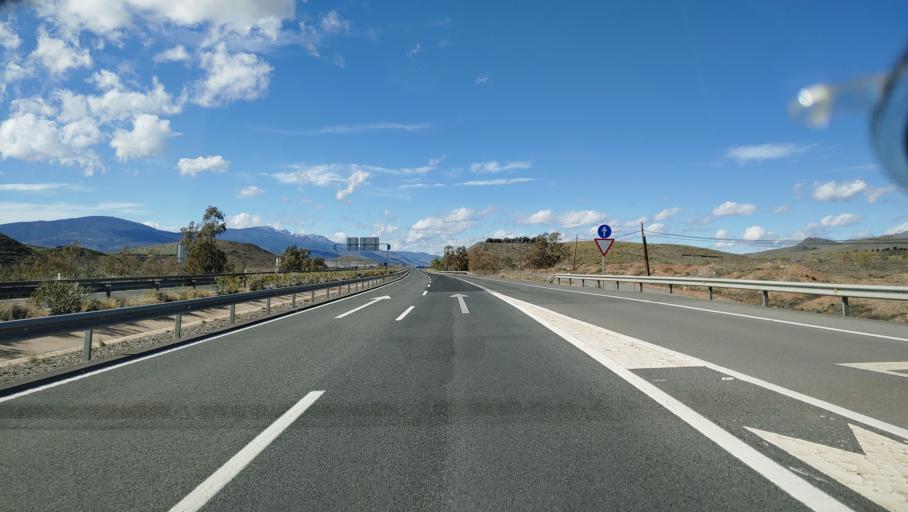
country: ES
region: Andalusia
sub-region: Provincia de Almeria
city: Gergal
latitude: 37.1168
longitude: -2.5545
